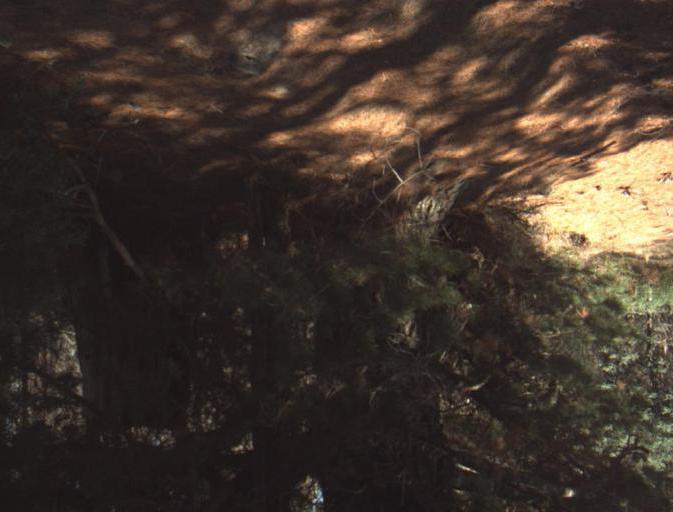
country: AU
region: Tasmania
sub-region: Dorset
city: Scottsdale
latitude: -41.2922
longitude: 147.3538
